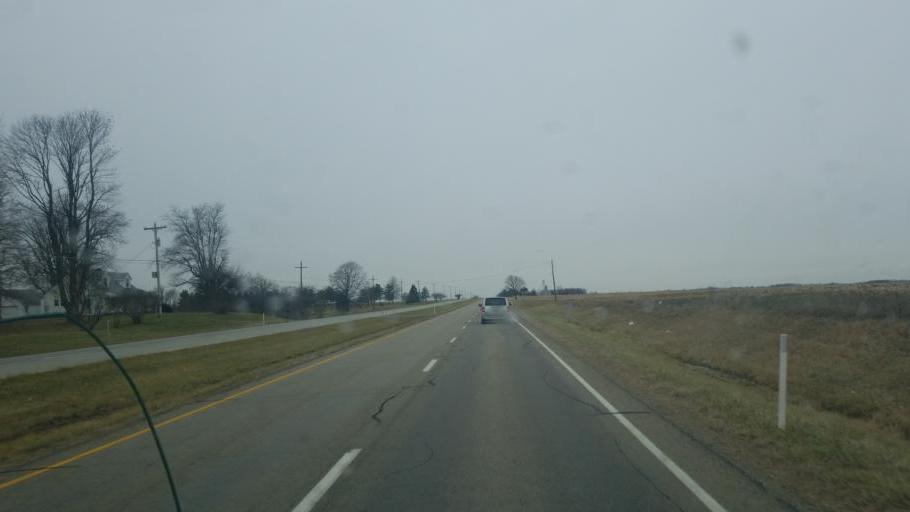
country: US
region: Indiana
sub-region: Henry County
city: Knightstown
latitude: 39.7930
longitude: -85.5696
